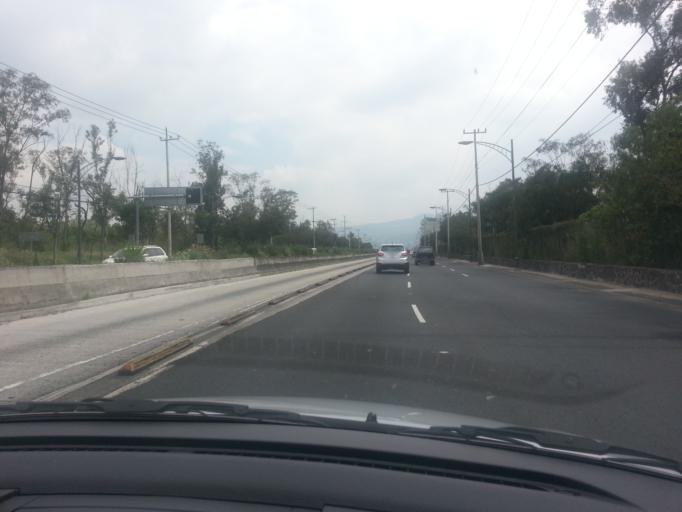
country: MX
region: Mexico City
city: Tlalpan
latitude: 19.3153
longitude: -99.1876
